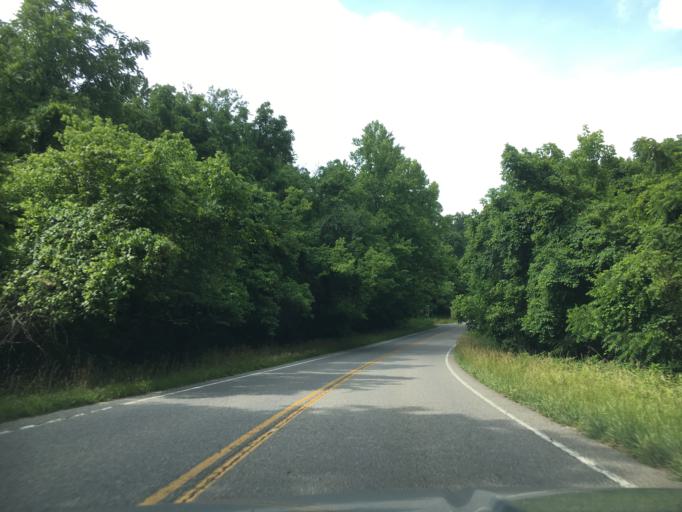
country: US
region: Virginia
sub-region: Roanoke County
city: Cave Spring
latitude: 37.1892
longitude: -80.0024
